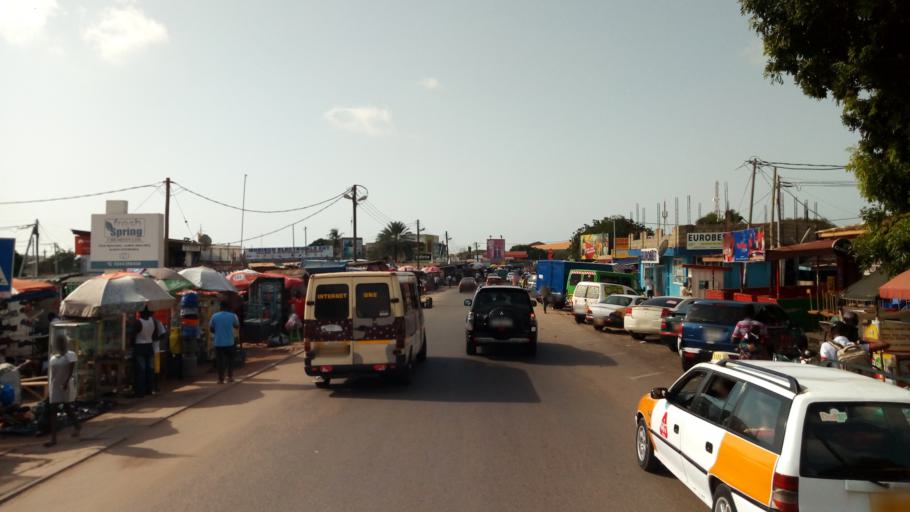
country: GH
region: Greater Accra
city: Tema
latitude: 5.6459
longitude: -0.0013
